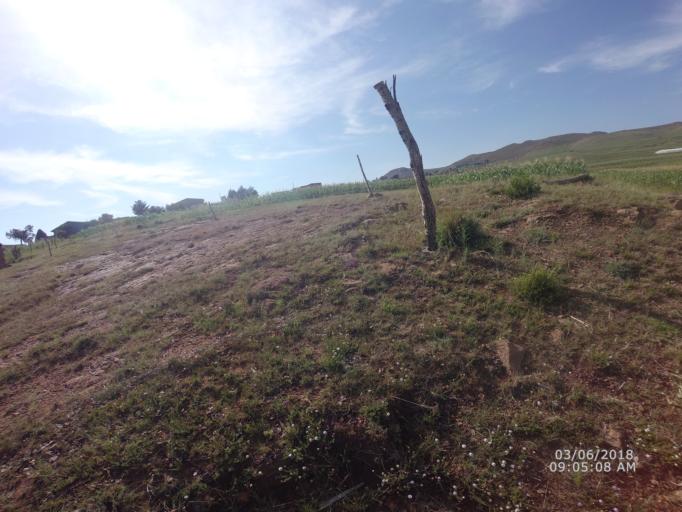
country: LS
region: Berea
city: Teyateyaneng
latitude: -29.2245
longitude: 27.8590
